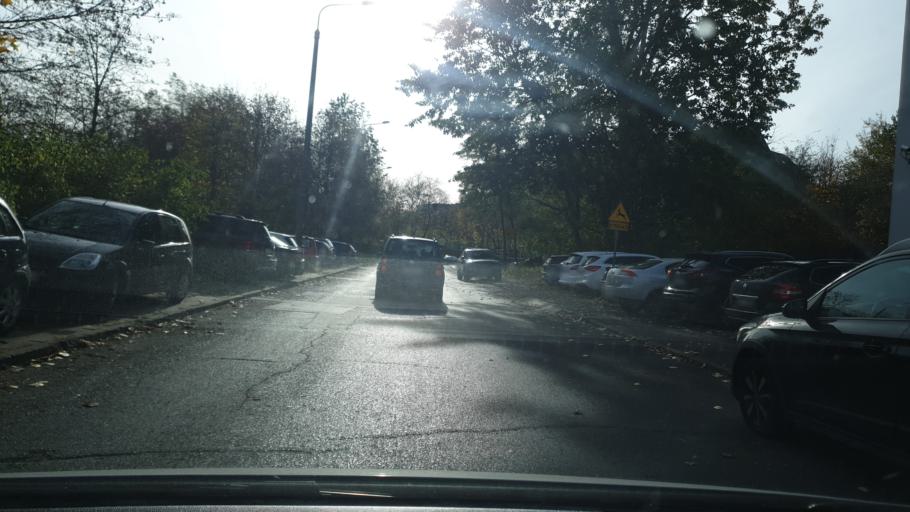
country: PL
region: Pomeranian Voivodeship
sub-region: Gdansk
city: Gdansk
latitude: 54.3640
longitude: 18.5886
